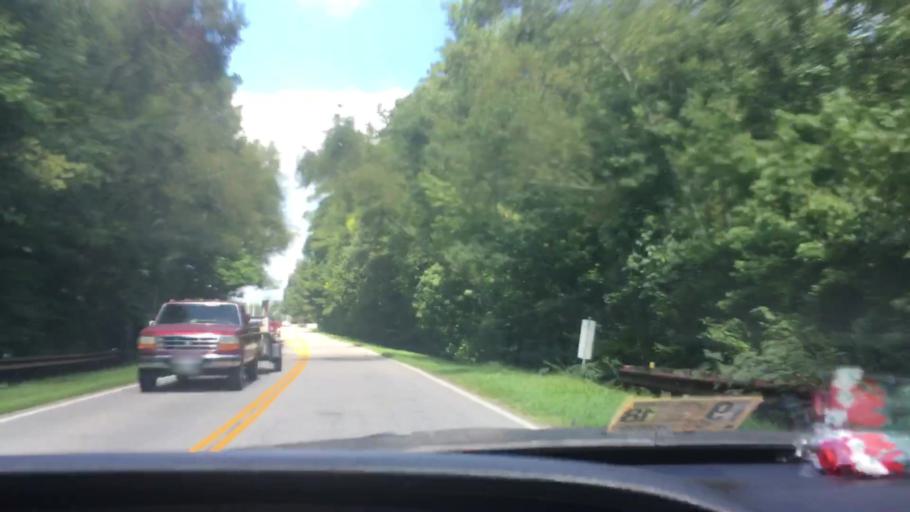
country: US
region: Virginia
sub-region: City of Chesapeake
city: Chesapeake
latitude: 36.7452
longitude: -76.1167
